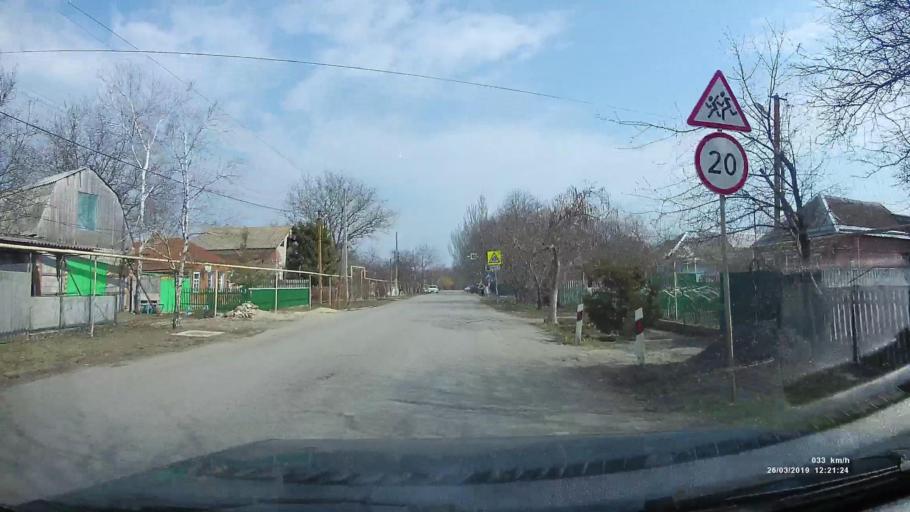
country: RU
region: Rostov
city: Novobessergenovka
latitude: 47.1508
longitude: 38.6616
